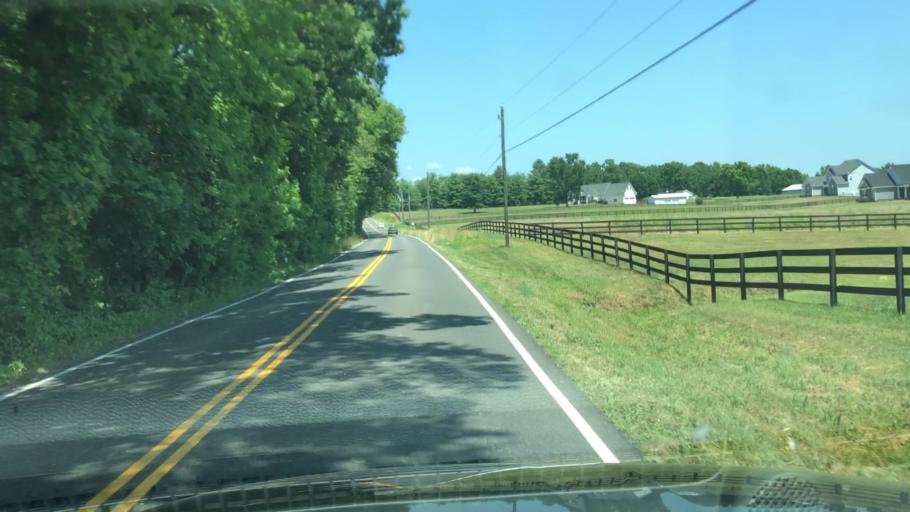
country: US
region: Virginia
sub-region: Stafford County
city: Falmouth
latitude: 38.4057
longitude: -77.5661
